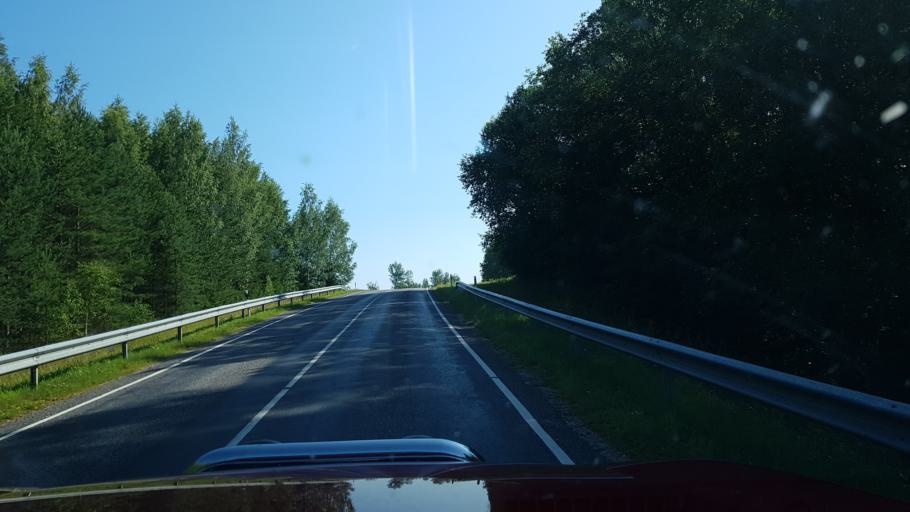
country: EE
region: Polvamaa
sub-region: Polva linn
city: Polva
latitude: 57.9863
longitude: 26.8861
